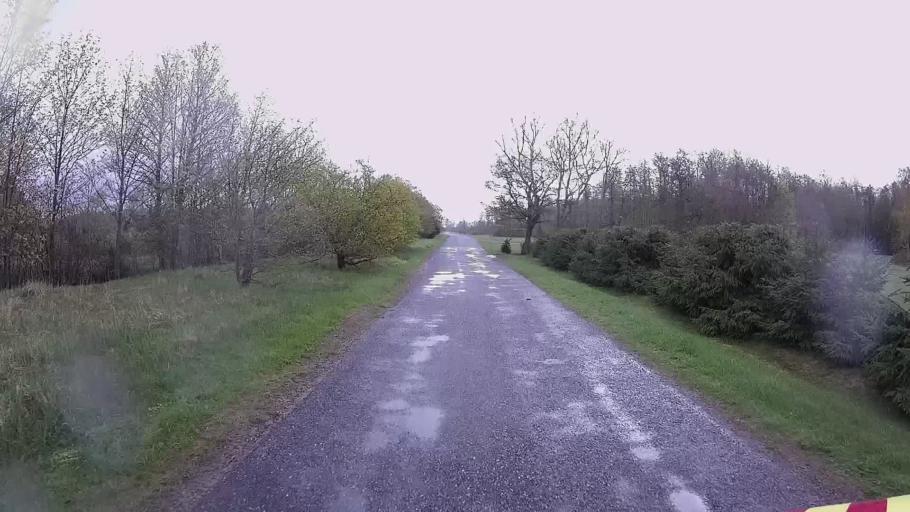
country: EE
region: Hiiumaa
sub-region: Kaerdla linn
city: Kardla
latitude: 58.6967
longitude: 22.5458
